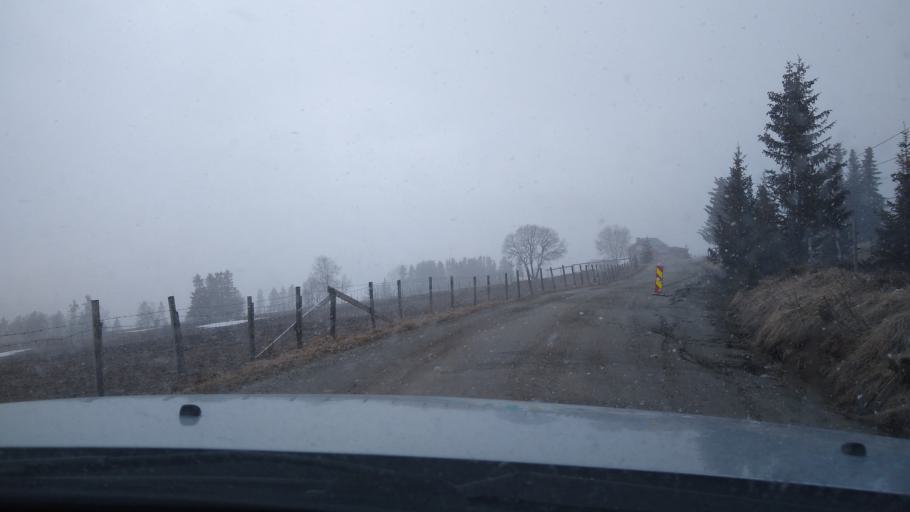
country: NO
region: Oppland
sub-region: Oyer
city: Tretten
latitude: 61.4612
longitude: 10.3404
